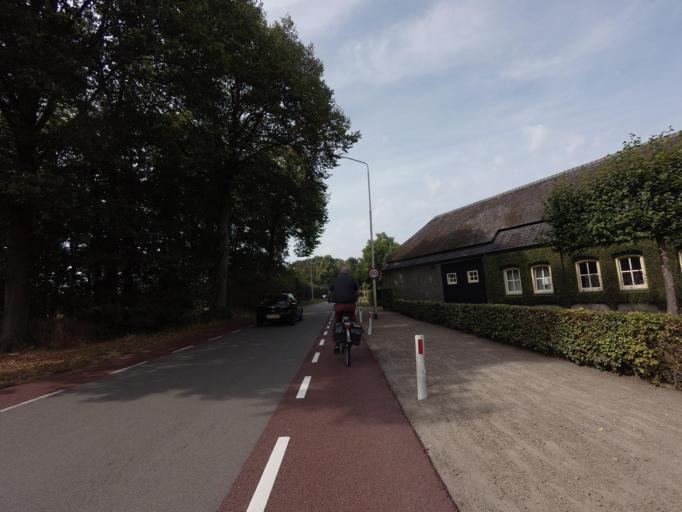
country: NL
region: North Brabant
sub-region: Gemeente Someren
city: Someren
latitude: 51.4185
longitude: 5.6930
